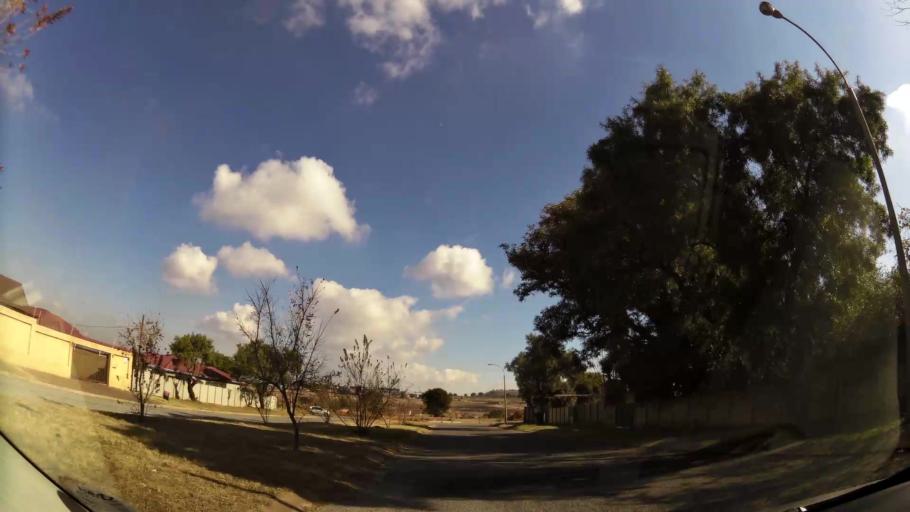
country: ZA
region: Gauteng
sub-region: City of Johannesburg Metropolitan Municipality
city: Roodepoort
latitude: -26.1524
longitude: 27.8217
